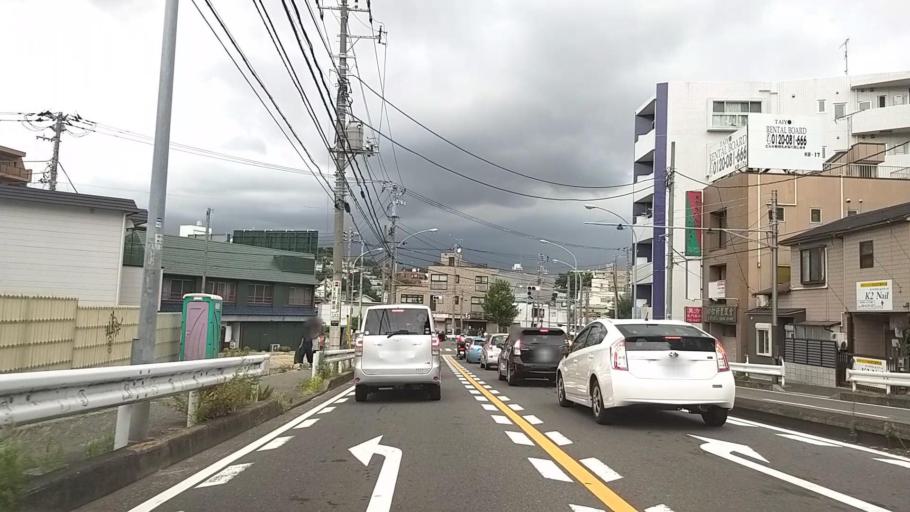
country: JP
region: Kanagawa
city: Yokohama
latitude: 35.4431
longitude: 139.5962
